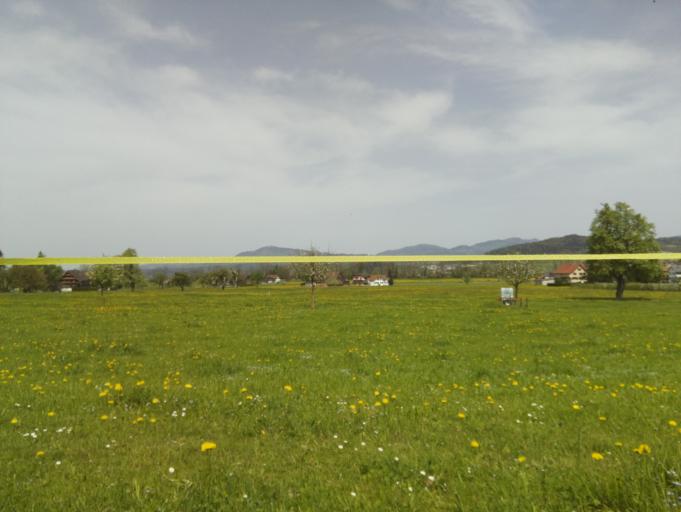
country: CH
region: Schwyz
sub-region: Bezirk March
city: Lachen
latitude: 47.1743
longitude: 8.8851
